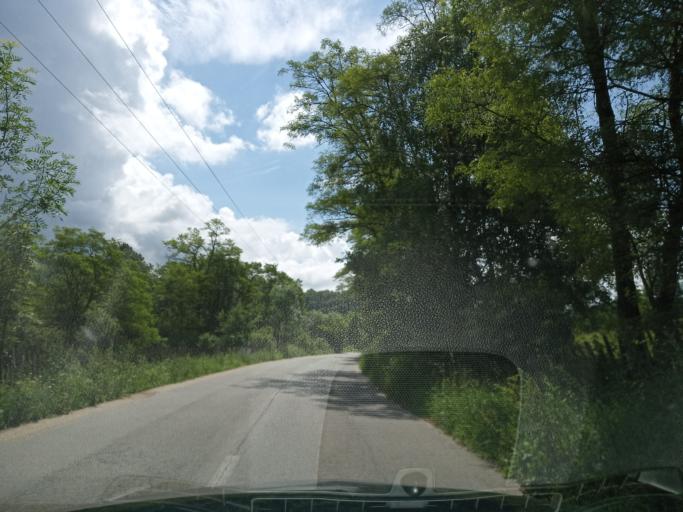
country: RO
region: Hunedoara
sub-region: Oras Petrila
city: Petrila
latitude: 45.4168
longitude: 23.4107
